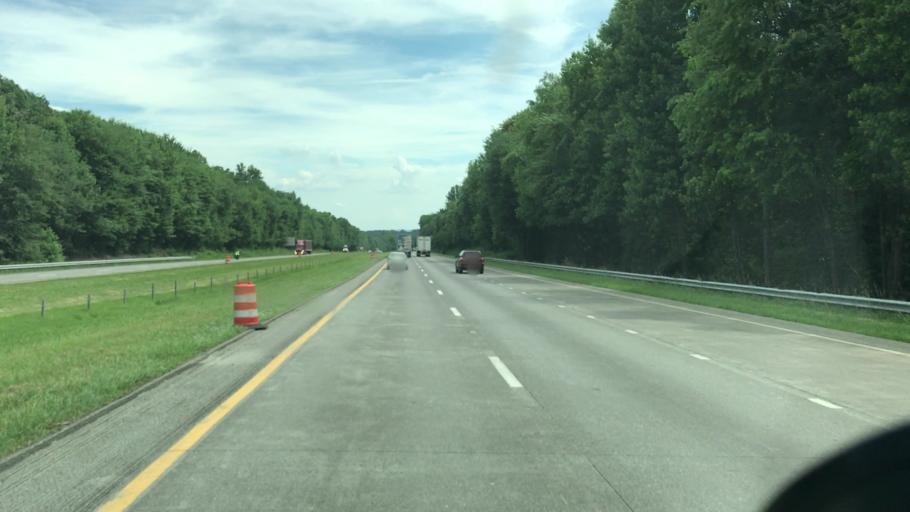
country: US
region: North Carolina
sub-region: Surry County
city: Dobson
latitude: 36.3879
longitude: -80.7889
